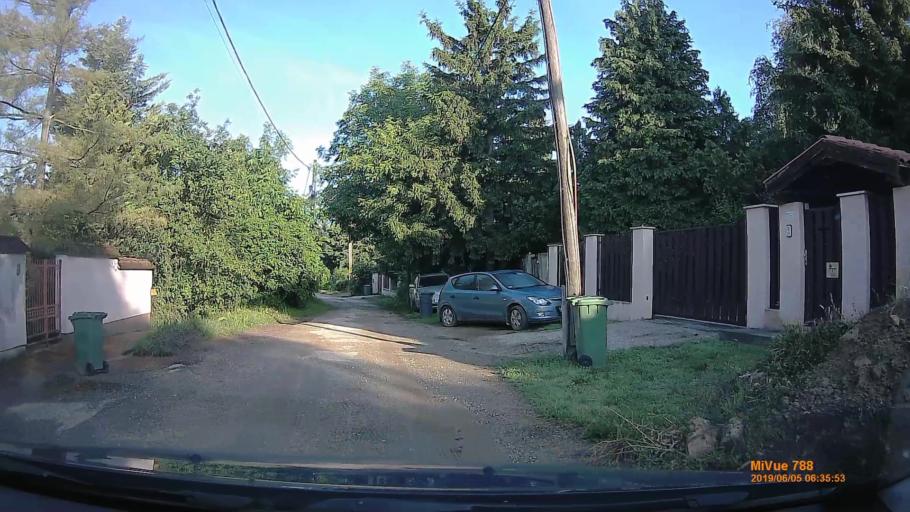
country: HU
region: Pest
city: Urom
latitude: 47.5757
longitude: 19.0204
